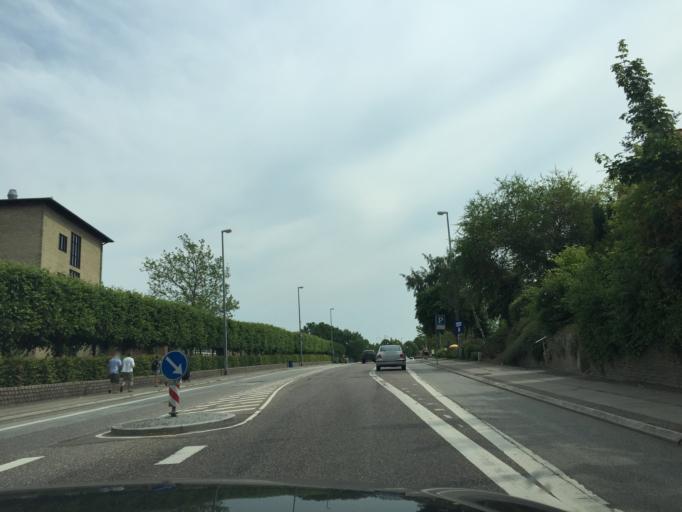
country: DK
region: Zealand
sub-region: Roskilde Kommune
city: Roskilde
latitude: 55.6363
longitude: 12.0884
